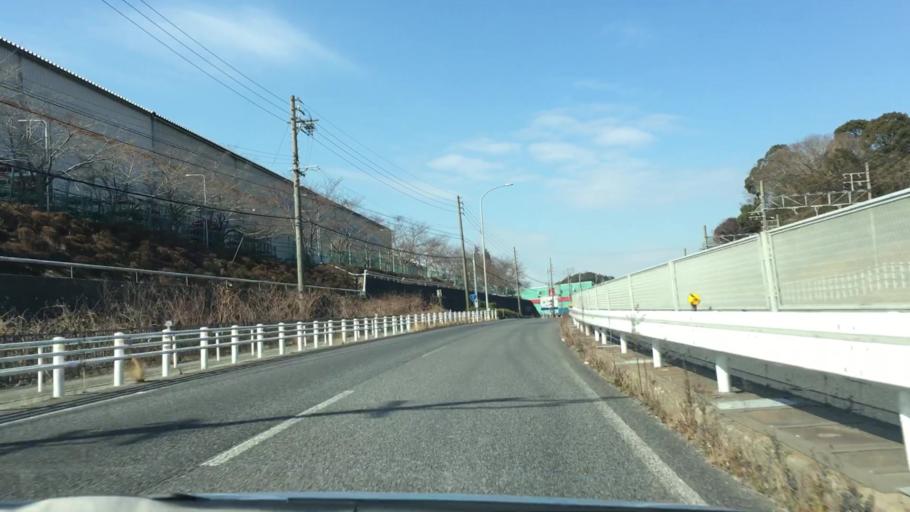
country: JP
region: Aichi
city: Gamagori
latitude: 34.8803
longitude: 137.2701
